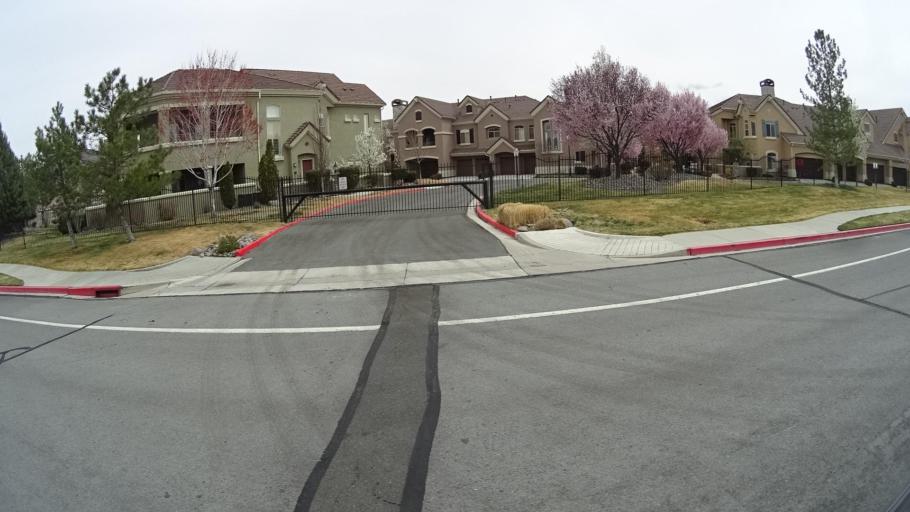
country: US
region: Nevada
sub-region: Washoe County
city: Sparks
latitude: 39.4408
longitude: -119.7358
